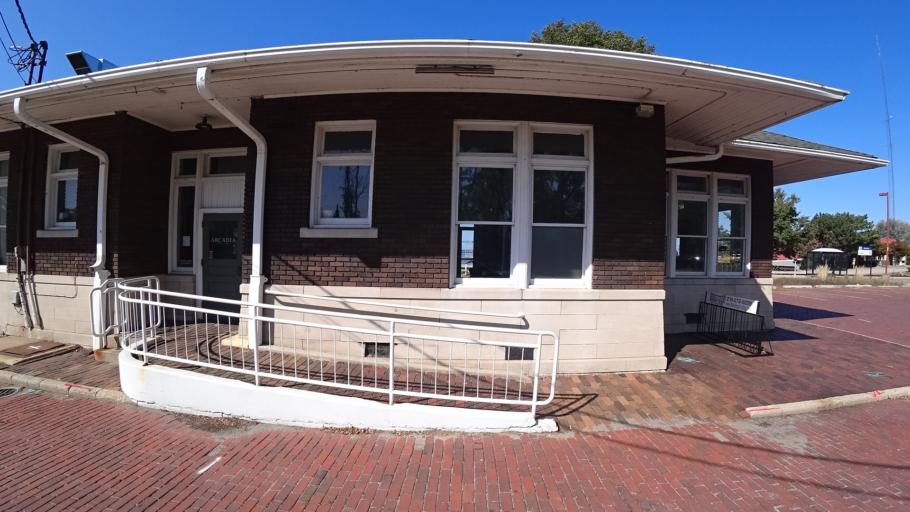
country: US
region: Indiana
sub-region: LaPorte County
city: Michigan City
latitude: 41.7208
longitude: -86.9056
